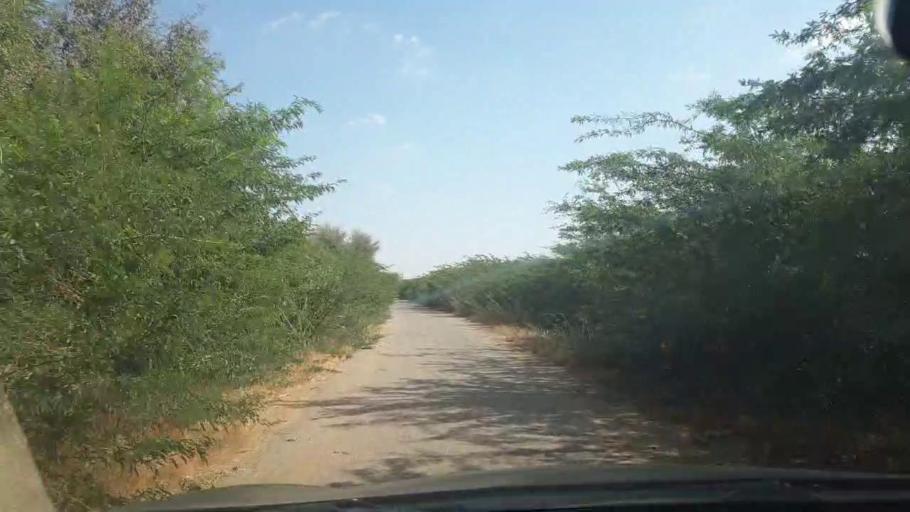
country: PK
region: Sindh
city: Malir Cantonment
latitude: 25.0589
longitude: 67.3931
